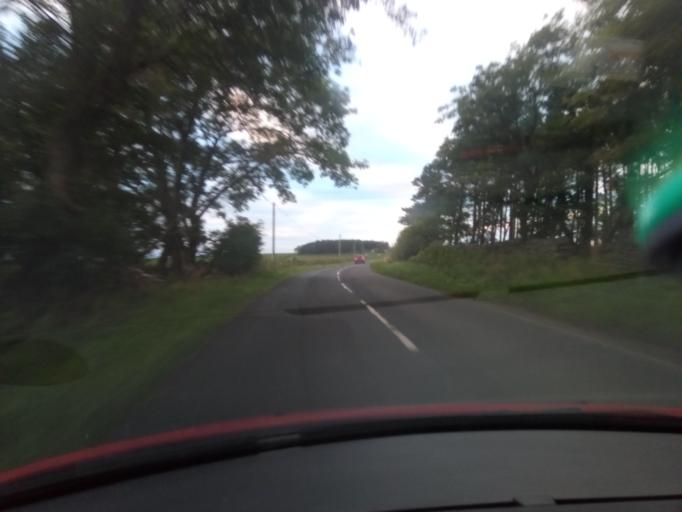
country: GB
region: England
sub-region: Northumberland
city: Bardon Mill
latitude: 54.9285
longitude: -2.3556
